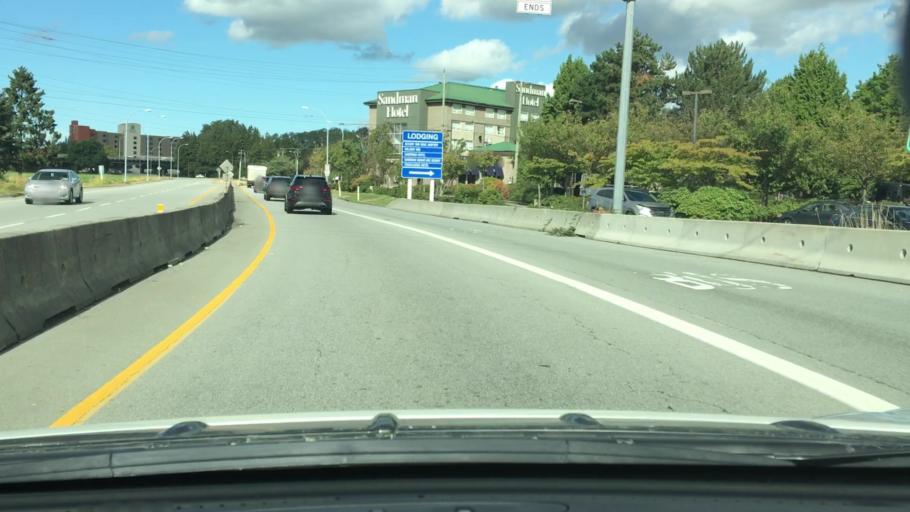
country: CA
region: British Columbia
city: Richmond
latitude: 49.1903
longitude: -123.1130
